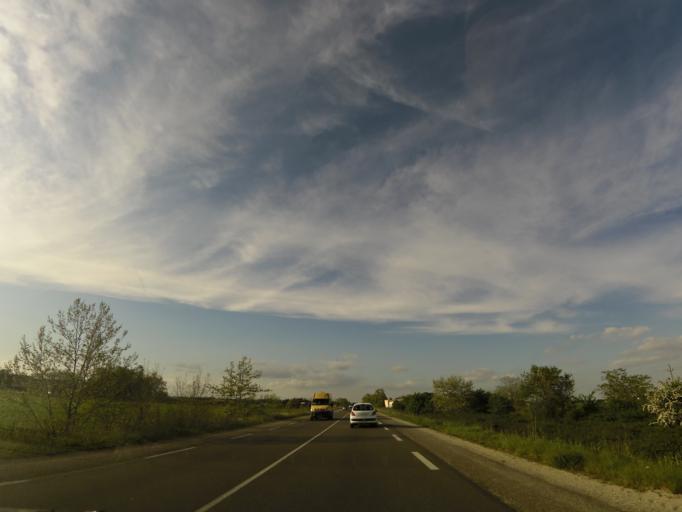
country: FR
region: Languedoc-Roussillon
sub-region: Departement de l'Herault
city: Saint-Just
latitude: 43.6481
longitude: 4.1394
